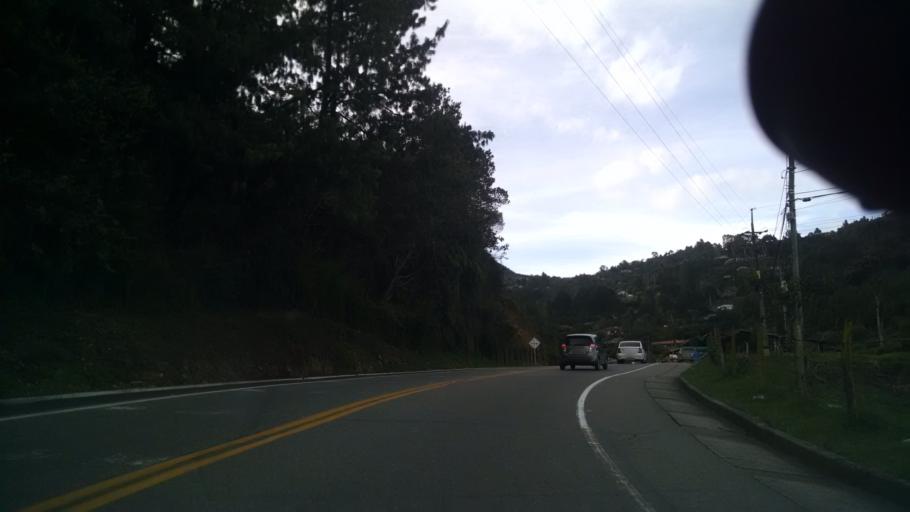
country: CO
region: Antioquia
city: El Retiro
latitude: 6.1266
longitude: -75.5013
